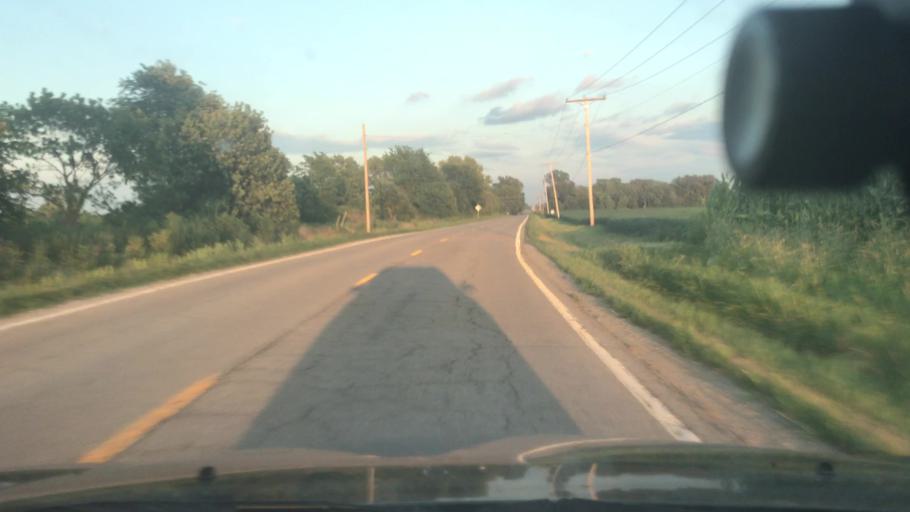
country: US
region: Illinois
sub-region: Washington County
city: Okawville
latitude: 38.4178
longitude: -89.5415
